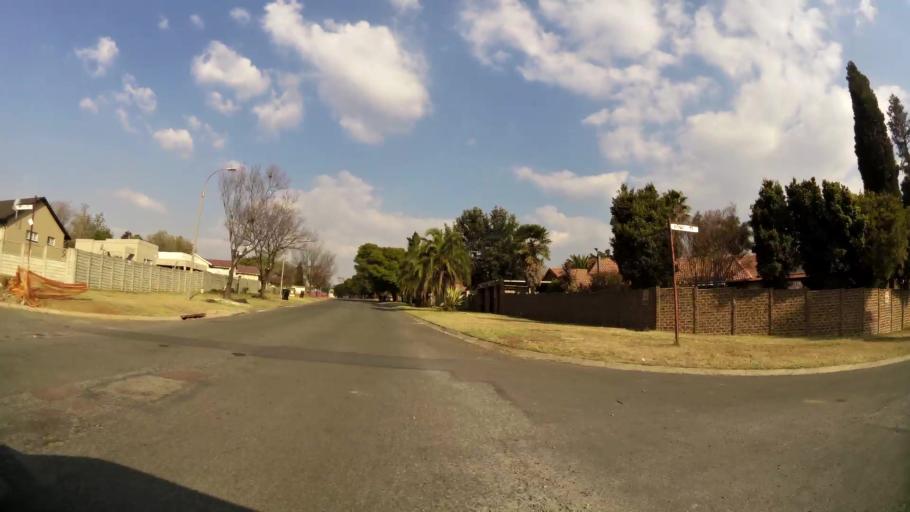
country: ZA
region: Gauteng
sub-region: City of Johannesburg Metropolitan Municipality
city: Modderfontein
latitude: -26.1043
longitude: 28.1878
